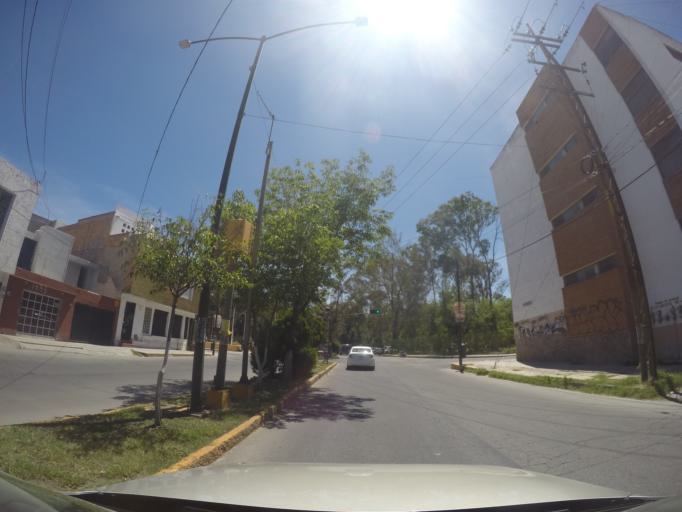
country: MX
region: San Luis Potosi
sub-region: San Luis Potosi
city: San Luis Potosi
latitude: 22.1511
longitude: -101.0144
